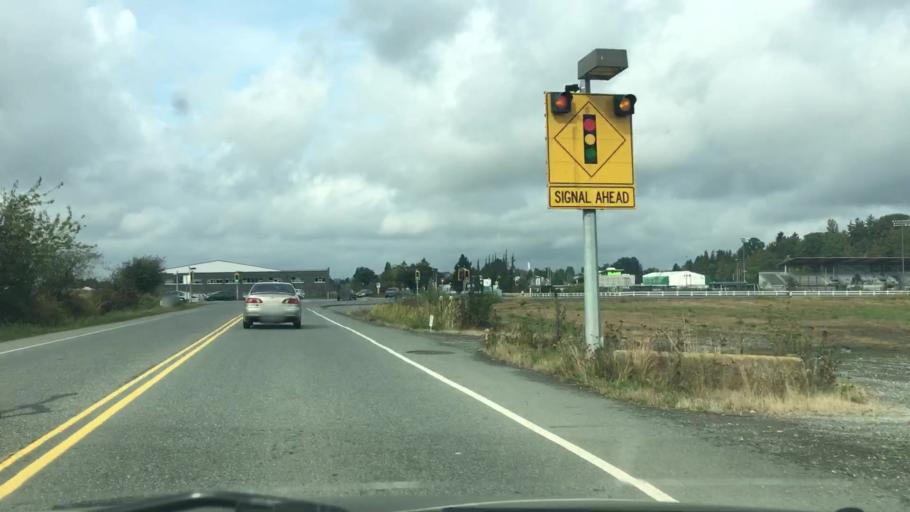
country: CA
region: British Columbia
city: Langley
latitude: 49.1040
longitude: -122.6229
